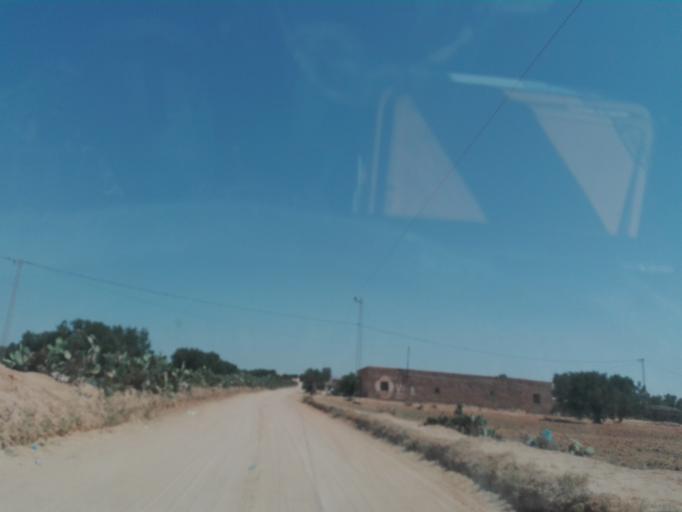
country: TN
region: Safaqis
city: Bi'r `Ali Bin Khalifah
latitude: 34.6632
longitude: 10.2394
